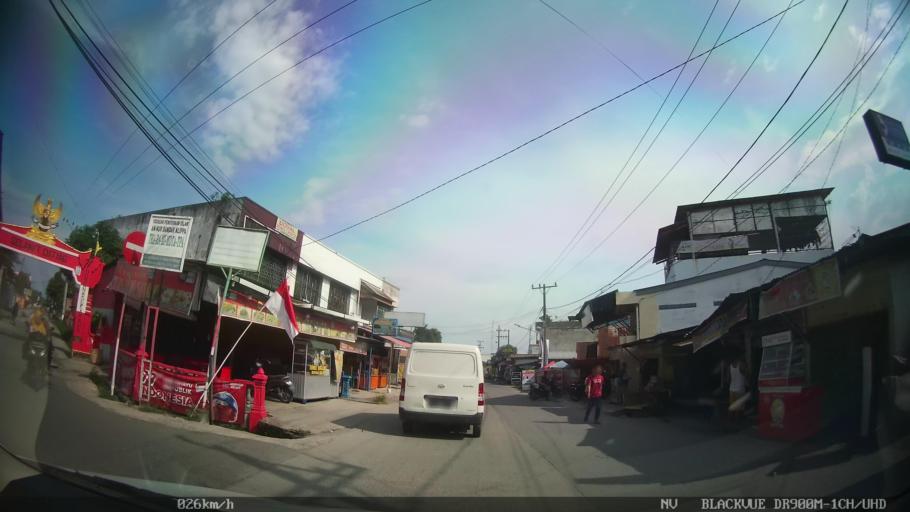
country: ID
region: North Sumatra
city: Medan
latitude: 3.5926
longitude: 98.7553
